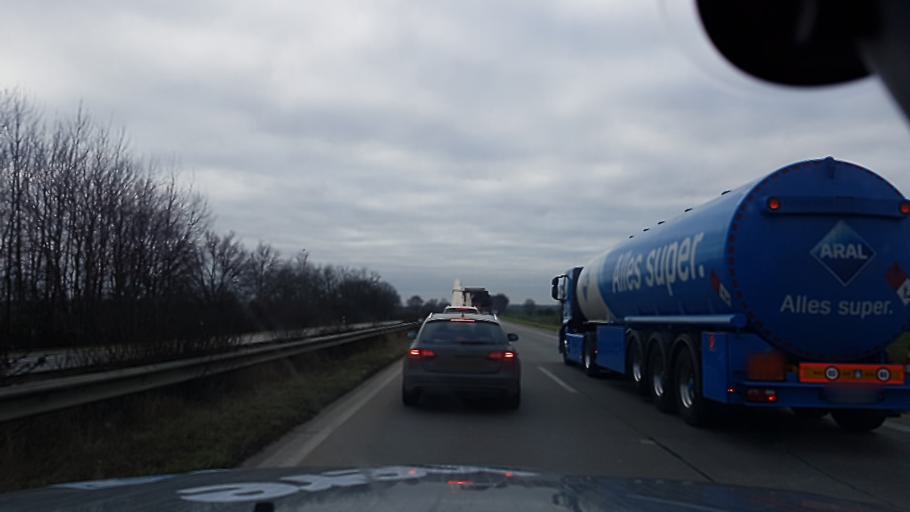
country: DE
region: Schleswig-Holstein
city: Ratekau
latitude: 53.9849
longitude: 10.7335
